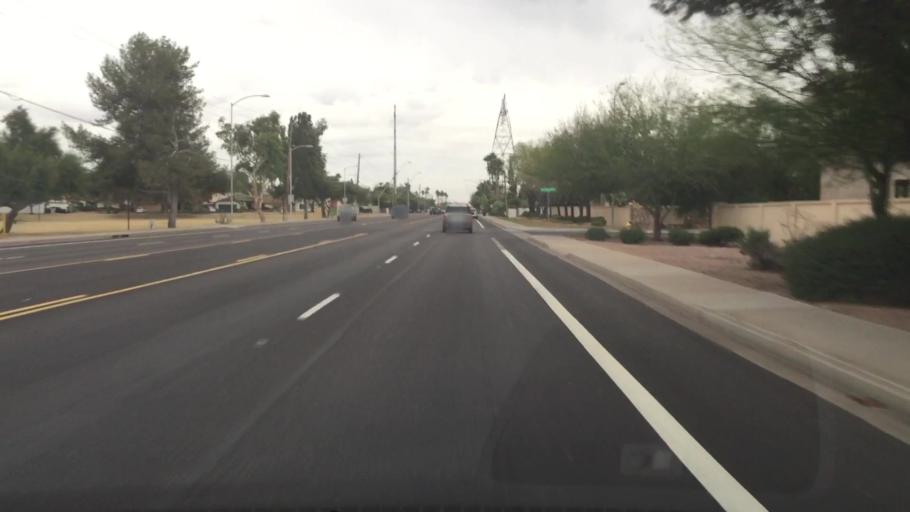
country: US
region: Arizona
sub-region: Maricopa County
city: Mesa
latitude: 33.4287
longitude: -111.7537
